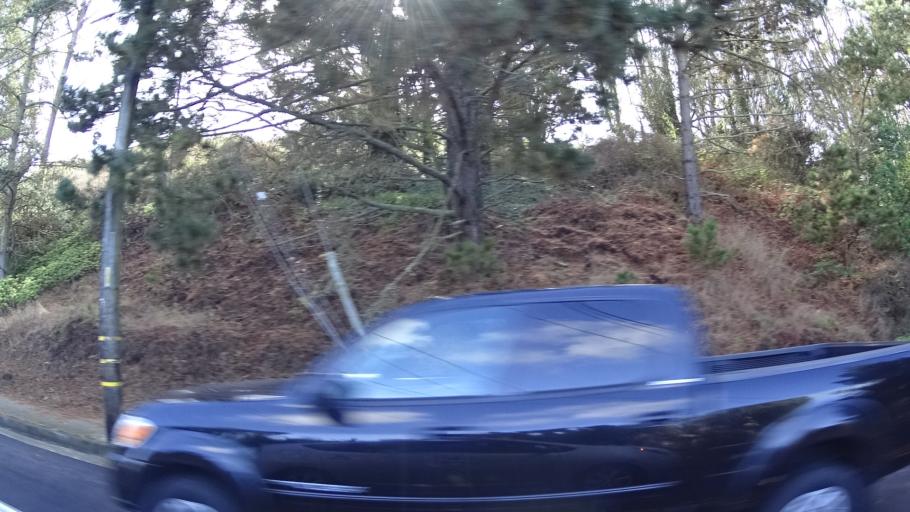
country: US
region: California
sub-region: San Mateo County
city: Daly City
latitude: 37.7024
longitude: -122.4539
